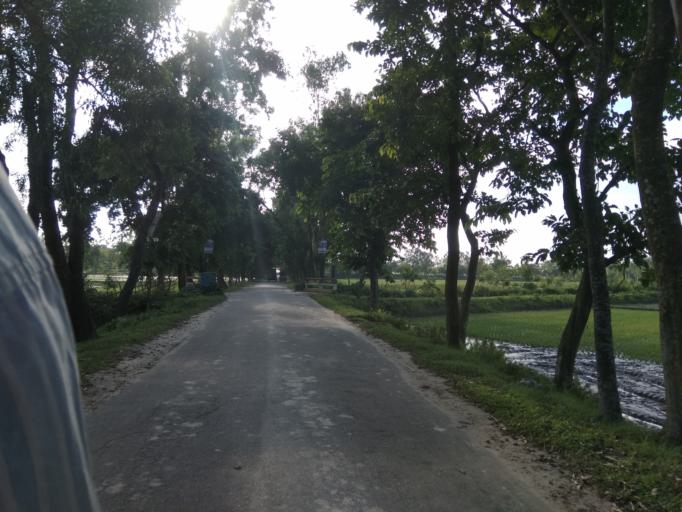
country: BD
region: Rangpur Division
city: Rangpur
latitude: 25.8312
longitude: 89.1165
